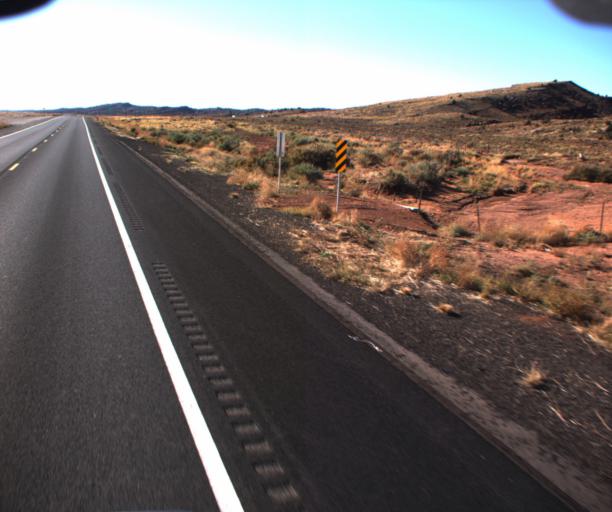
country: US
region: Arizona
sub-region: Coconino County
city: LeChee
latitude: 36.4769
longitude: -111.5725
